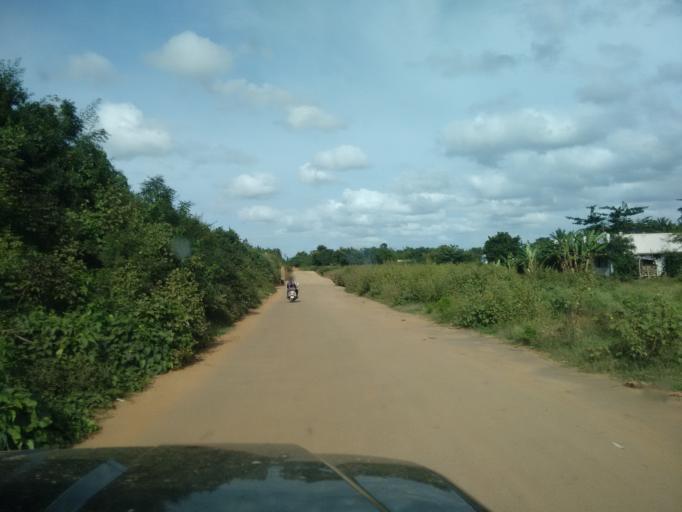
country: IN
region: Karnataka
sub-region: Tumkur
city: Gubbi
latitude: 13.3222
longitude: 76.9442
